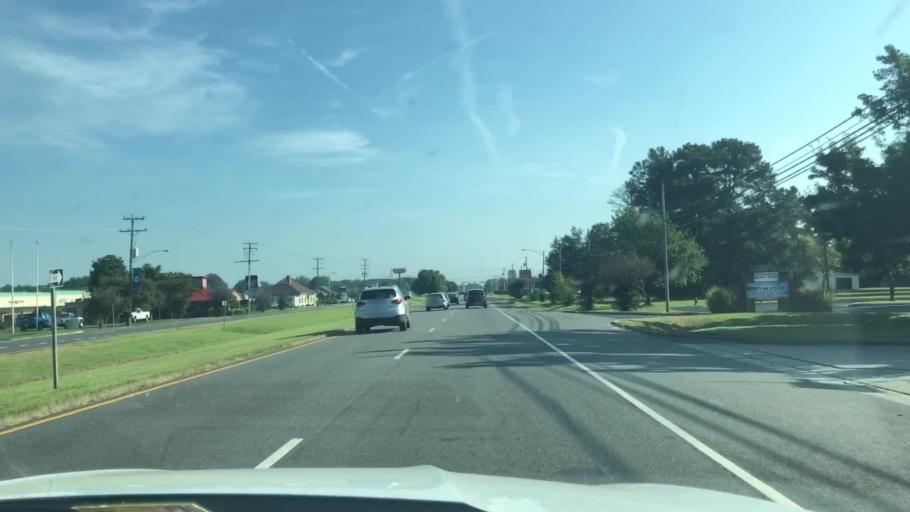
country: US
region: Virginia
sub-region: Essex County
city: Tappahannock
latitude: 37.9000
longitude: -76.8692
